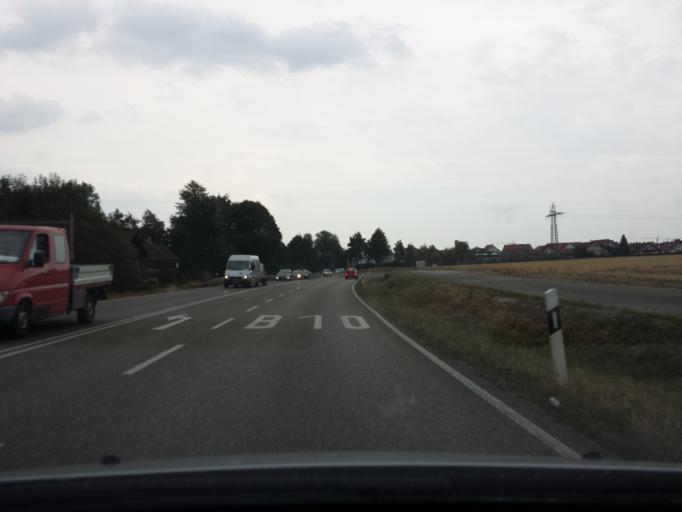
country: DE
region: Bavaria
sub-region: Swabia
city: Nersingen
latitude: 48.4229
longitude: 10.1121
